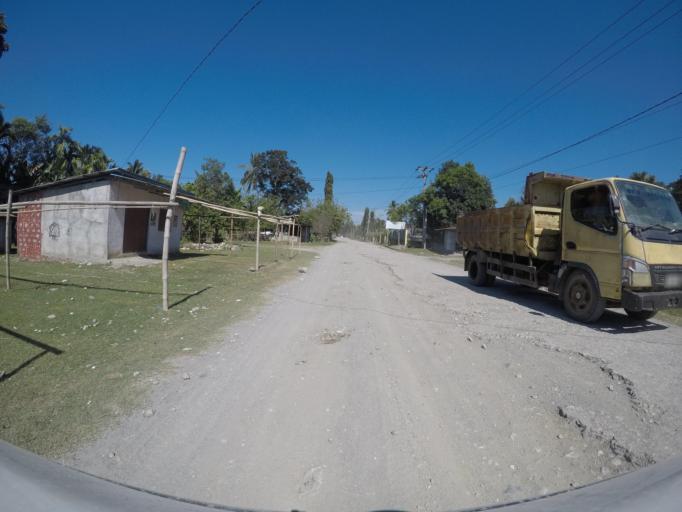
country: TL
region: Viqueque
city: Viqueque
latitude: -8.9763
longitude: 126.0454
